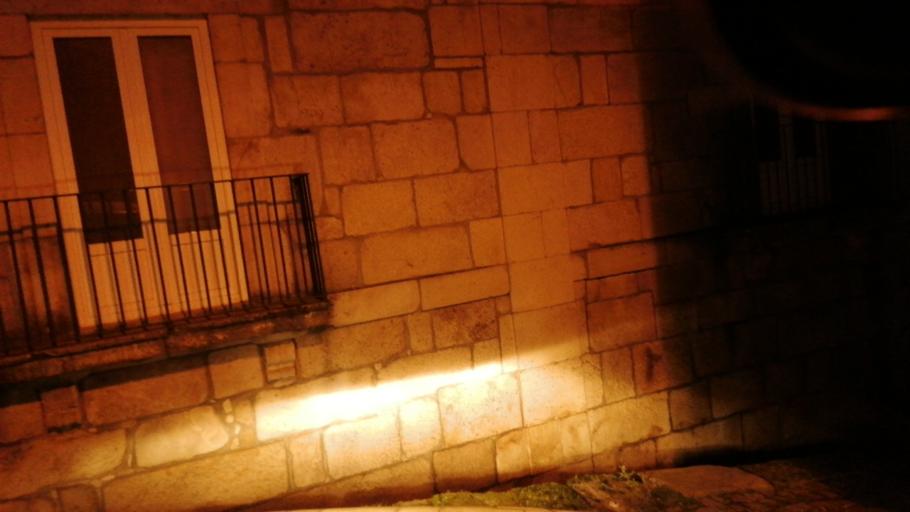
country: PT
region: Vila Real
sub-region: Sabrosa
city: Sabrosa
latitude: 41.2670
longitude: -7.4983
